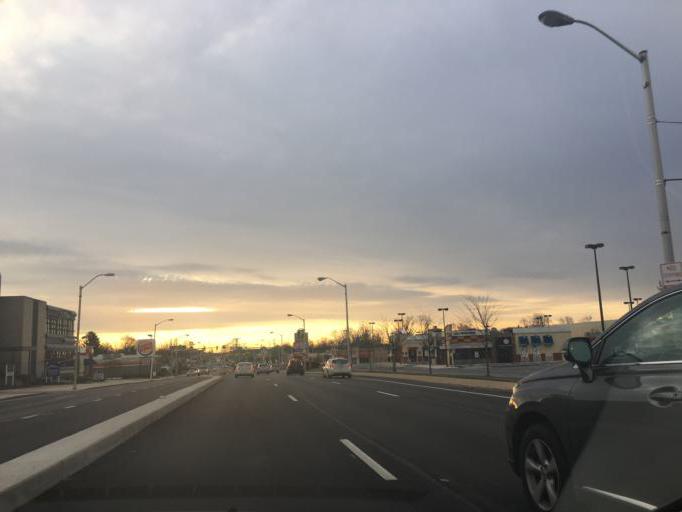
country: US
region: Maryland
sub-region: Baltimore County
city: Pikesville
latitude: 39.3579
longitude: -76.7048
